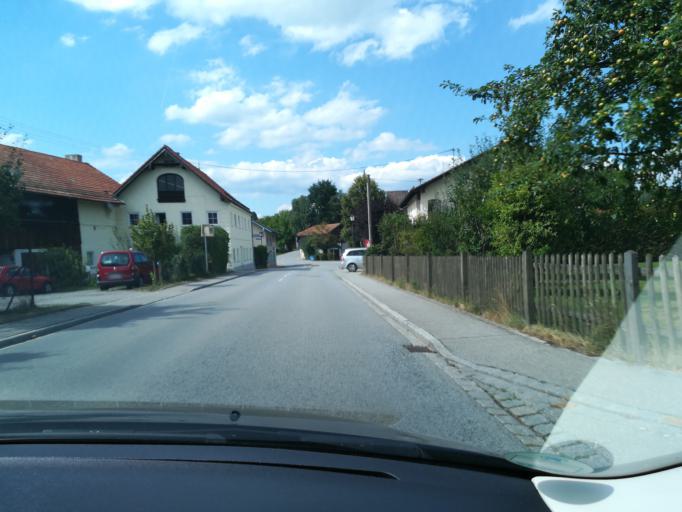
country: DE
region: Bavaria
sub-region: Upper Bavaria
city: Assling
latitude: 47.9746
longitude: 11.9584
